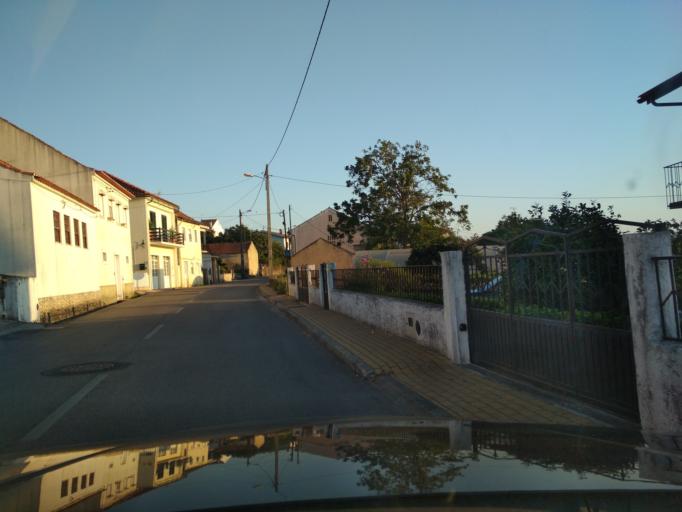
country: PT
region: Coimbra
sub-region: Coimbra
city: Coimbra
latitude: 40.2372
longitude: -8.4086
